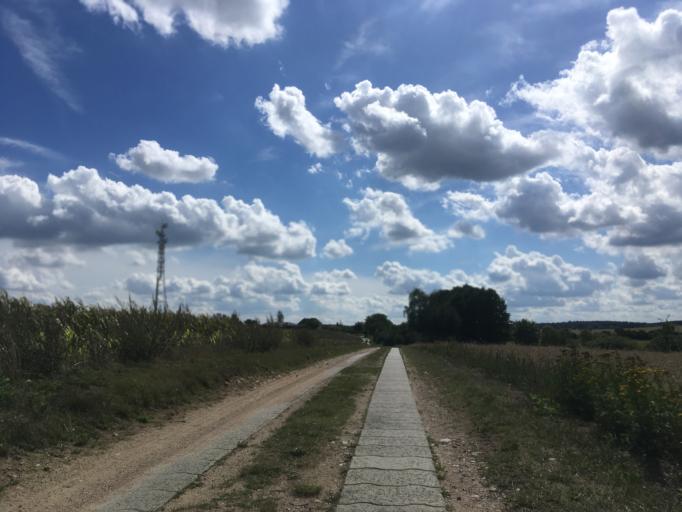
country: DE
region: Brandenburg
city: Gerswalde
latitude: 53.0980
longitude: 13.8689
